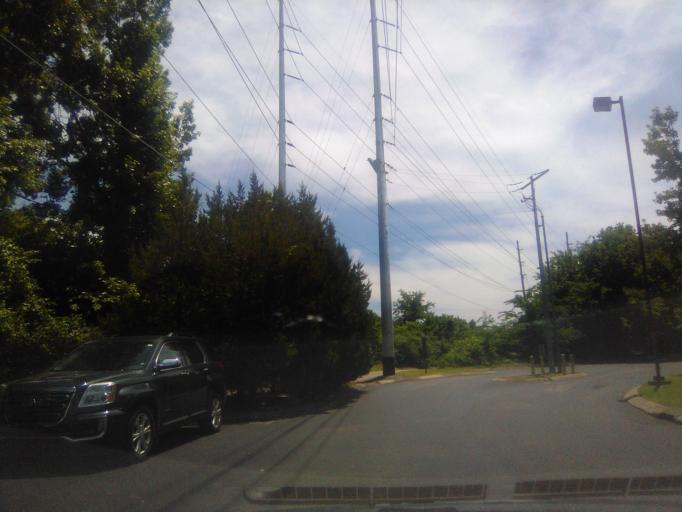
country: US
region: Tennessee
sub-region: Davidson County
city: Belle Meade
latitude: 36.1288
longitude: -86.8485
